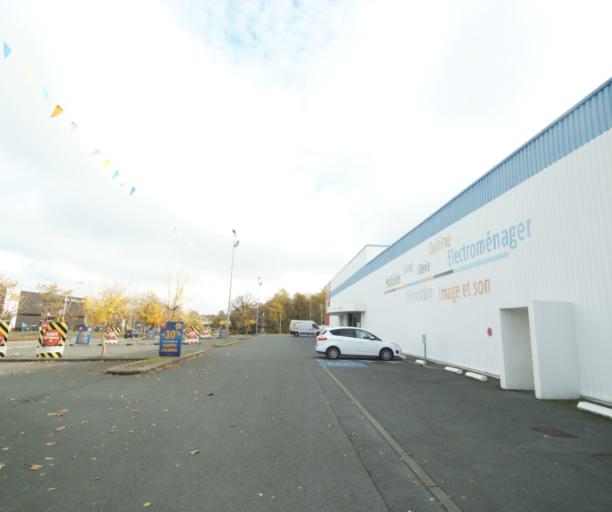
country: FR
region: Poitou-Charentes
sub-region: Departement de la Charente-Maritime
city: Saintes
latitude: 45.7489
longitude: -0.6753
